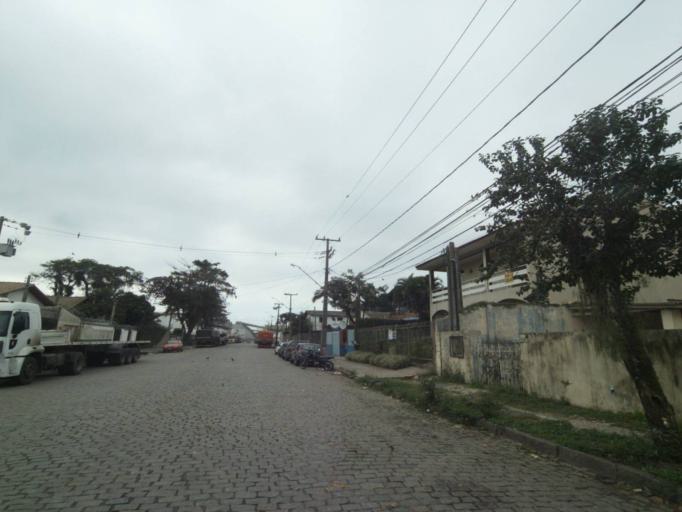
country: BR
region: Parana
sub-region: Paranagua
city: Paranagua
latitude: -25.5122
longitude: -48.5164
